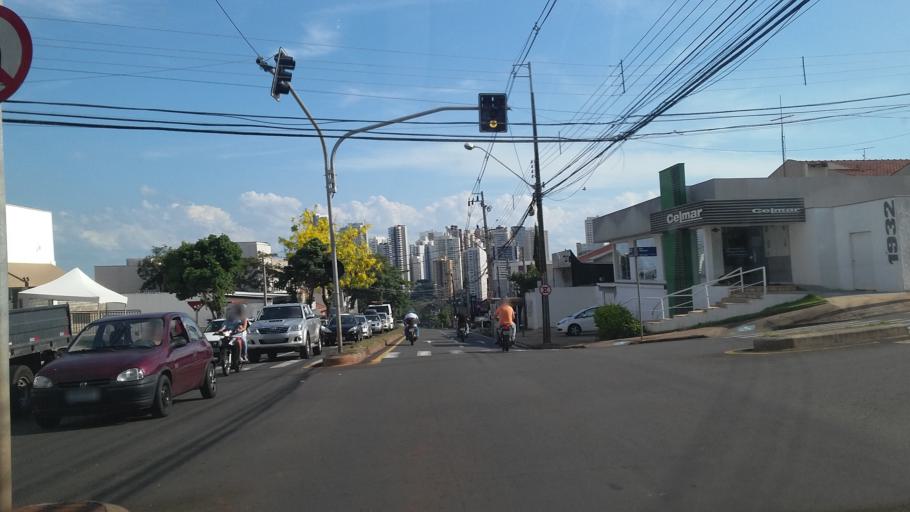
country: BR
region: Parana
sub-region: Londrina
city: Londrina
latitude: -23.3186
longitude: -51.1768
